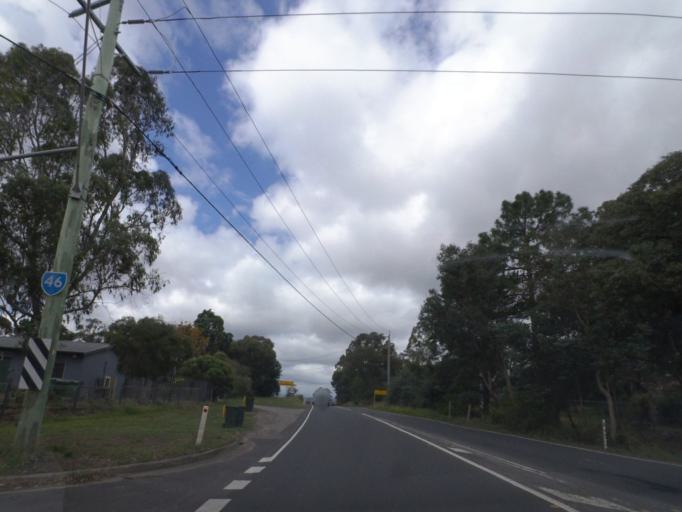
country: AU
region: Victoria
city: Plenty
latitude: -37.6776
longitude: 145.1275
